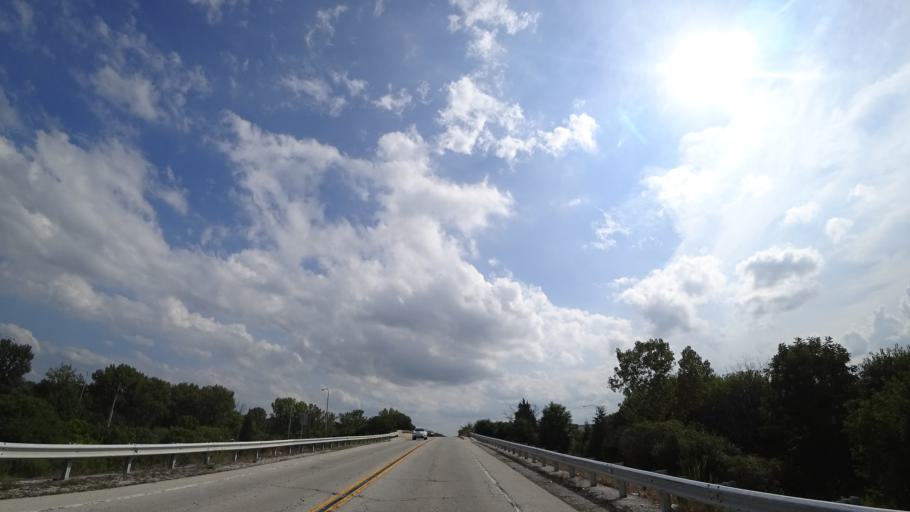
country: US
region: Illinois
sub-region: Cook County
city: Tinley Park
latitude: 41.5545
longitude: -87.7712
